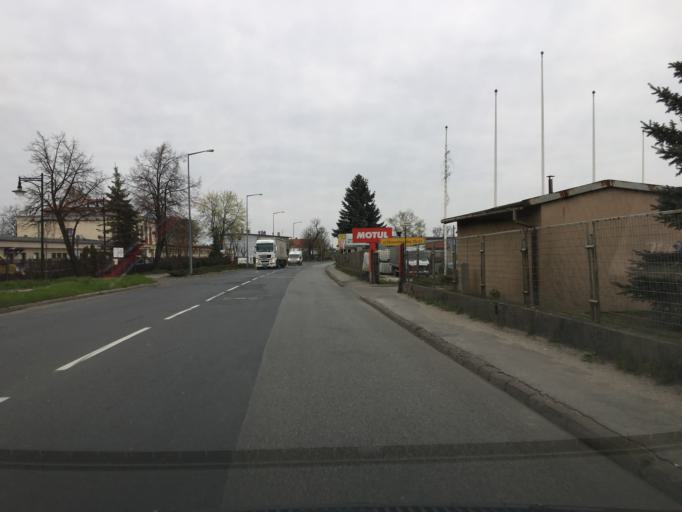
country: PL
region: Lower Silesian Voivodeship
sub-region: Legnica
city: Legnica
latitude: 51.1818
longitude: 16.1590
